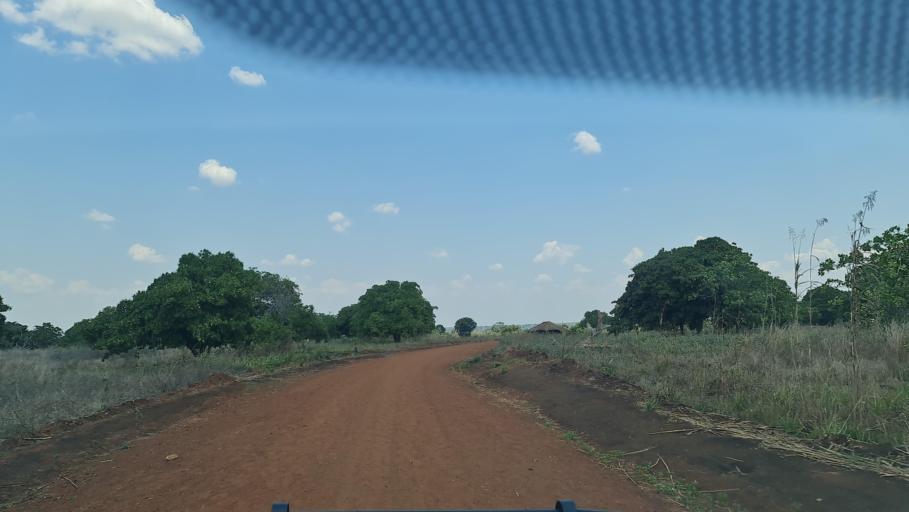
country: MZ
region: Nampula
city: Nacala
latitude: -14.8146
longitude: 40.0731
